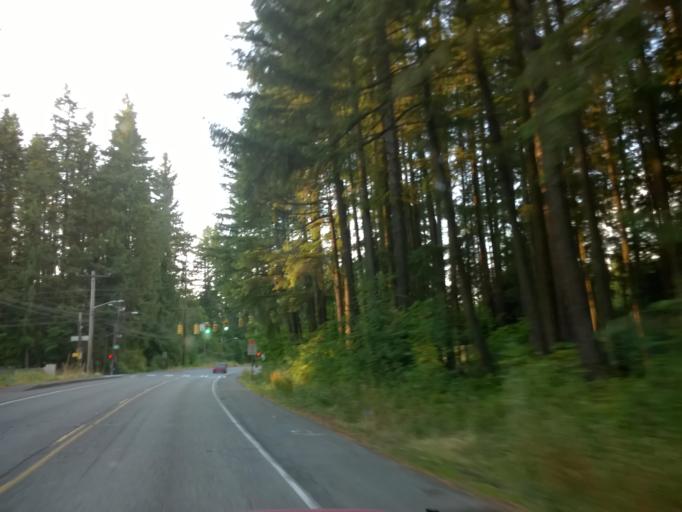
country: US
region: Washington
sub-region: King County
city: Cottage Lake
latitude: 47.7476
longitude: -122.0820
